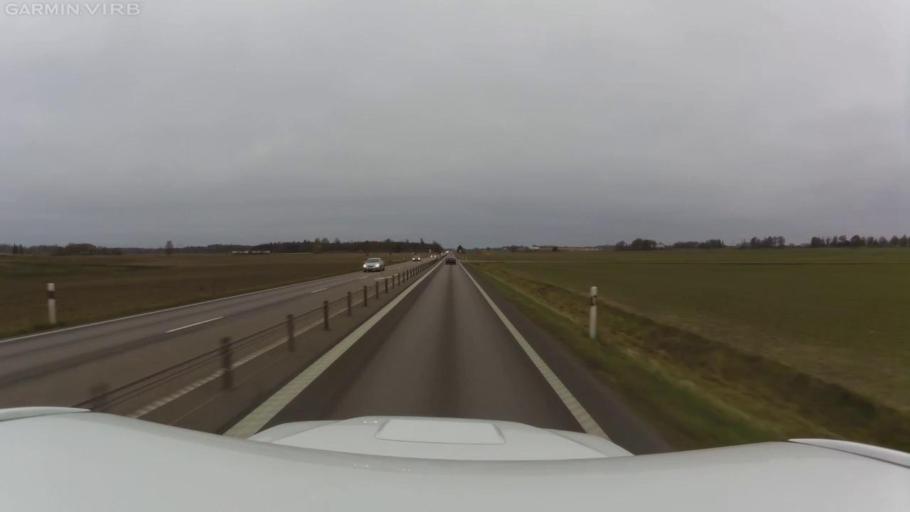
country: SE
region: OEstergoetland
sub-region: Linkopings Kommun
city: Vikingstad
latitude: 58.3753
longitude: 15.4677
